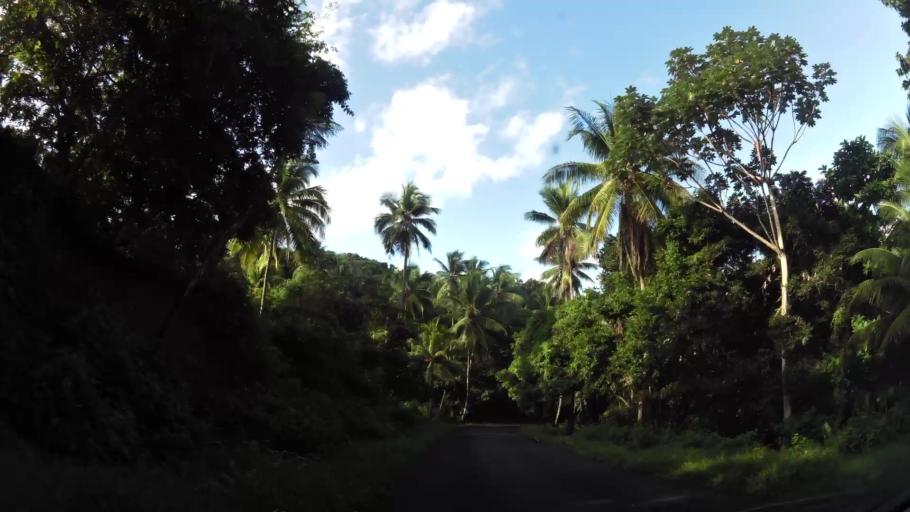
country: DM
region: Saint Andrew
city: Calibishie
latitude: 15.5893
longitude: -61.3710
